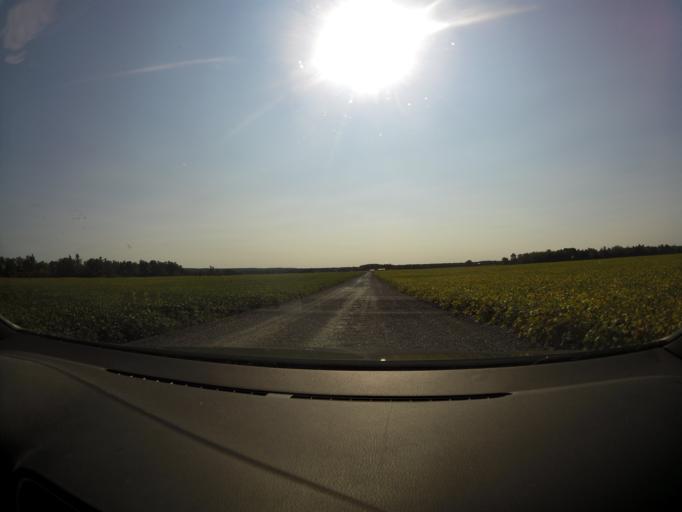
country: CA
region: Ontario
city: Arnprior
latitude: 45.3870
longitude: -76.3493
